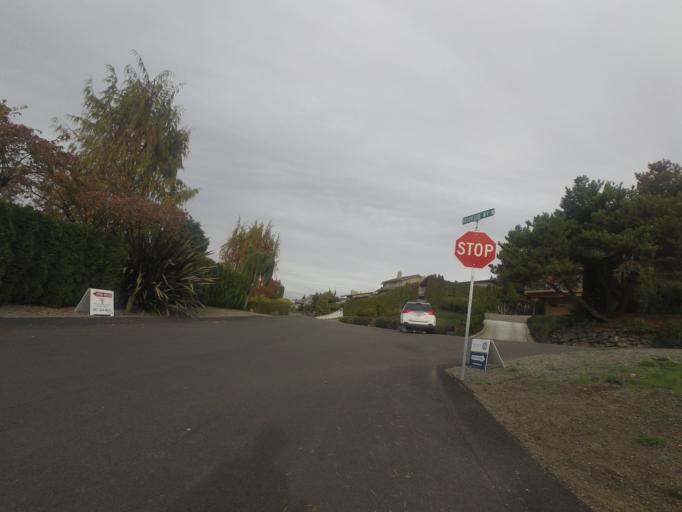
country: US
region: Washington
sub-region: Pierce County
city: University Place
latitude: 47.2258
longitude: -122.5625
